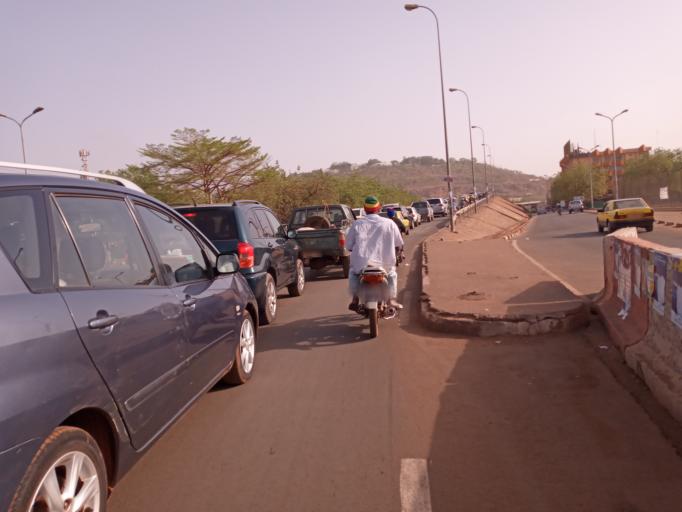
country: ML
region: Bamako
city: Bamako
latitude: 12.6468
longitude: -8.0096
